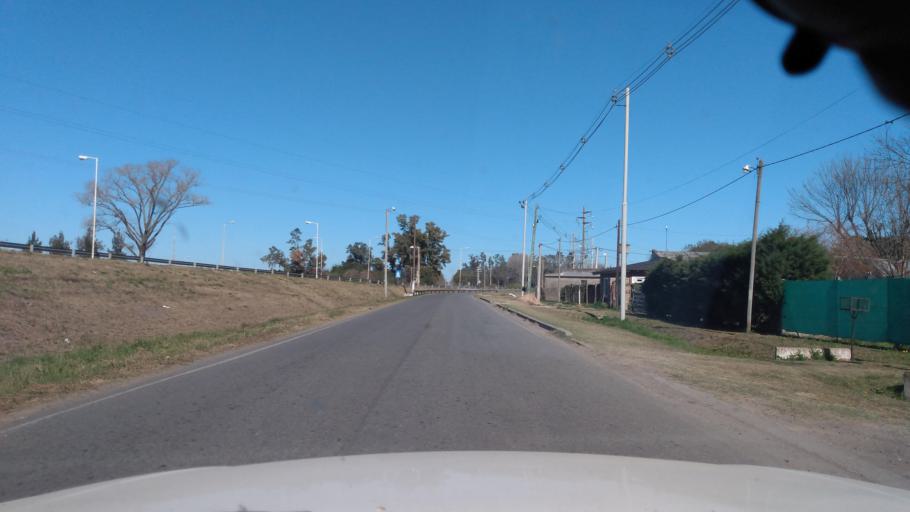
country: AR
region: Buenos Aires
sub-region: Partido de Mercedes
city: Mercedes
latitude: -34.6554
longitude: -59.3555
